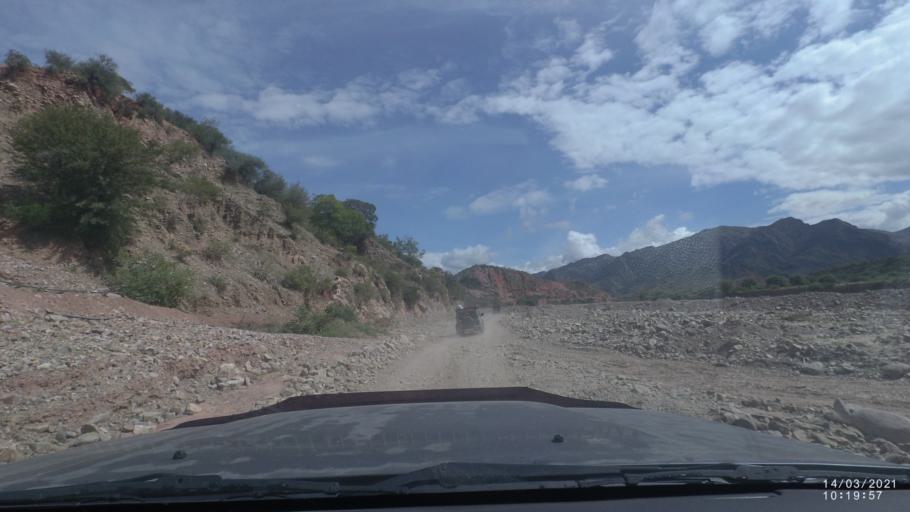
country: BO
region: Cochabamba
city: Cliza
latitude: -17.9306
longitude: -65.8704
